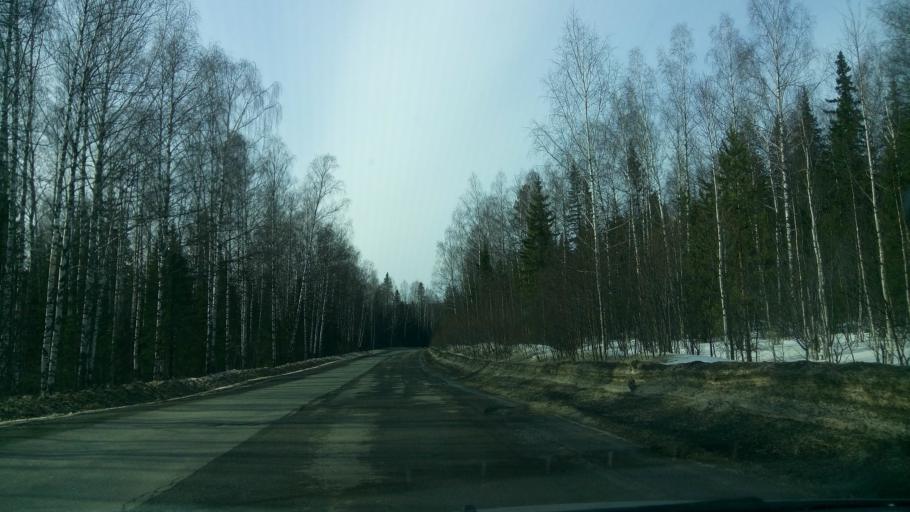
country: RU
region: Sverdlovsk
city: Uralets
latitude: 57.6863
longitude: 59.7284
